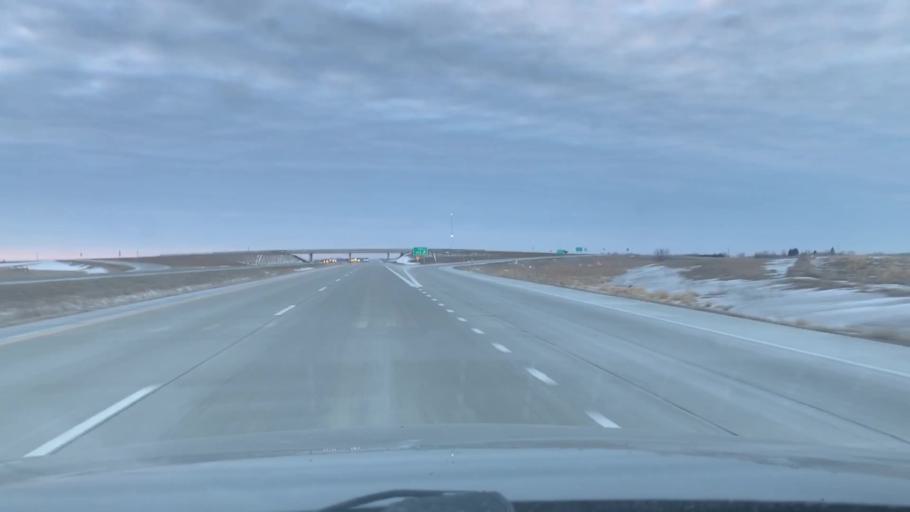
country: US
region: North Dakota
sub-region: Barnes County
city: Valley City
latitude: 46.9201
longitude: -97.7817
